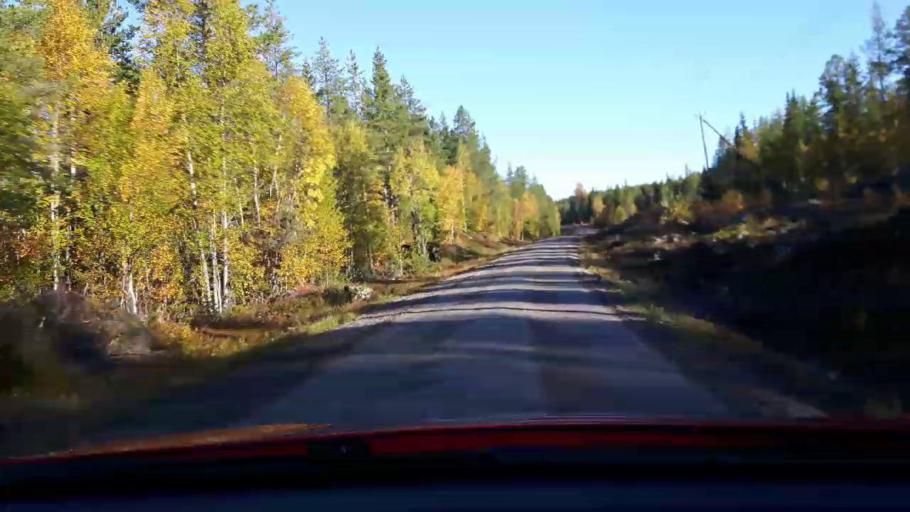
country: SE
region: Jaemtland
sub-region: Stroemsunds Kommun
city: Stroemsund
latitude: 64.3911
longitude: 15.1496
